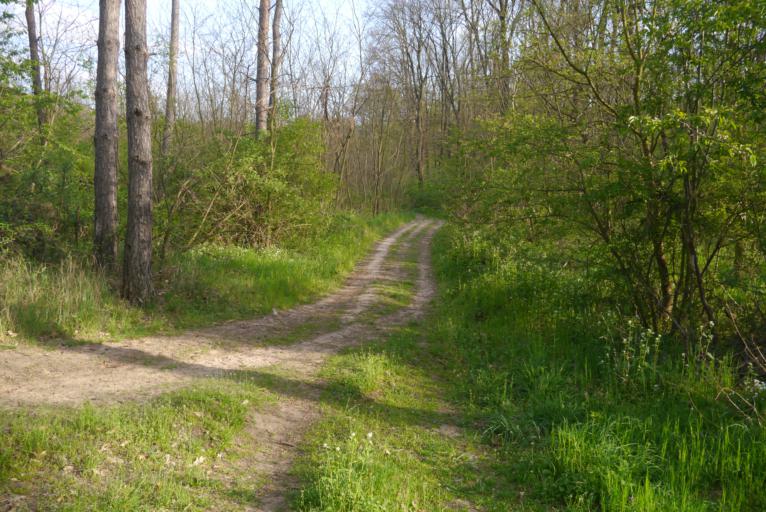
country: HU
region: Pest
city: Piliscsaba
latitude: 47.6508
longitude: 18.8246
